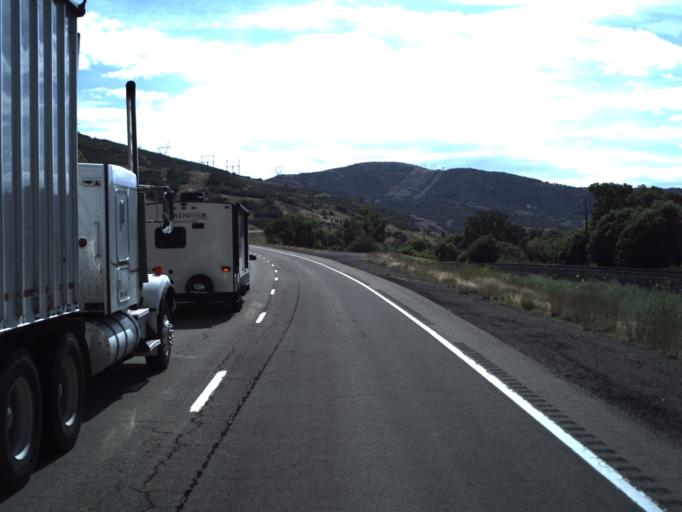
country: US
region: Utah
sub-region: Utah County
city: Mapleton
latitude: 40.0347
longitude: -111.5232
